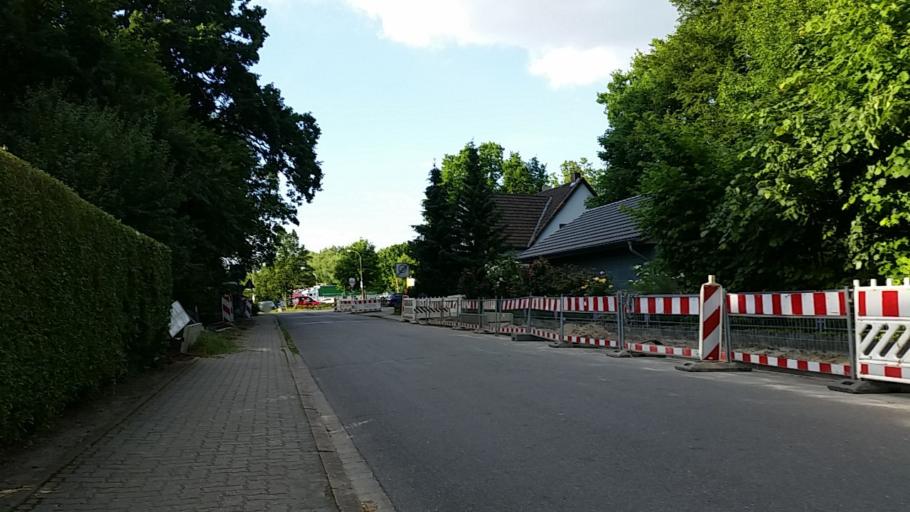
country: DE
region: Lower Saxony
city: Weyhausen
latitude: 52.3928
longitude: 10.7160
